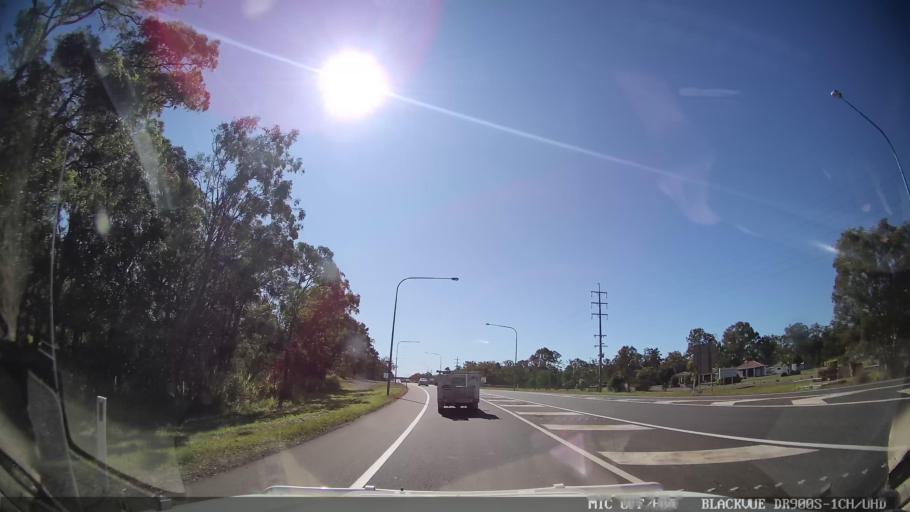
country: AU
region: Queensland
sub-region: Fraser Coast
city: Maryborough
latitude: -25.5128
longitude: 152.6712
